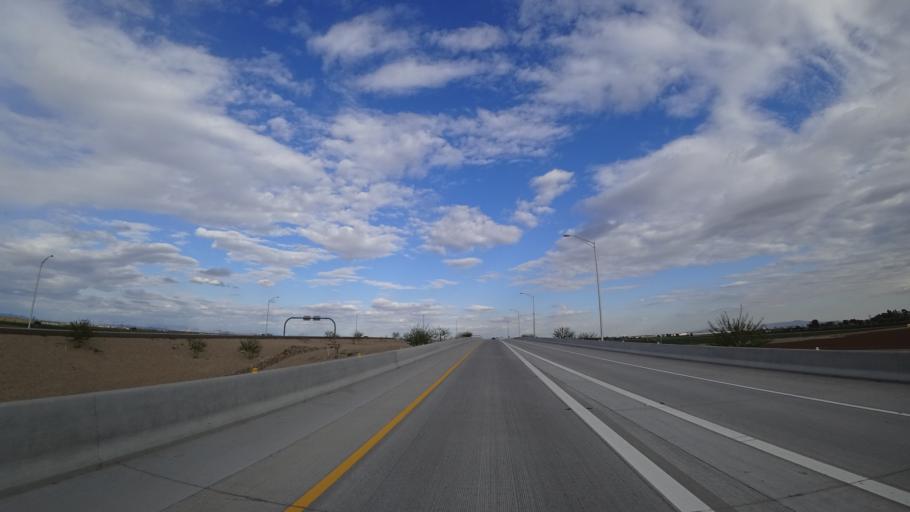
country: US
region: Arizona
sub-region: Maricopa County
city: Citrus Park
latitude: 33.5588
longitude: -112.4122
